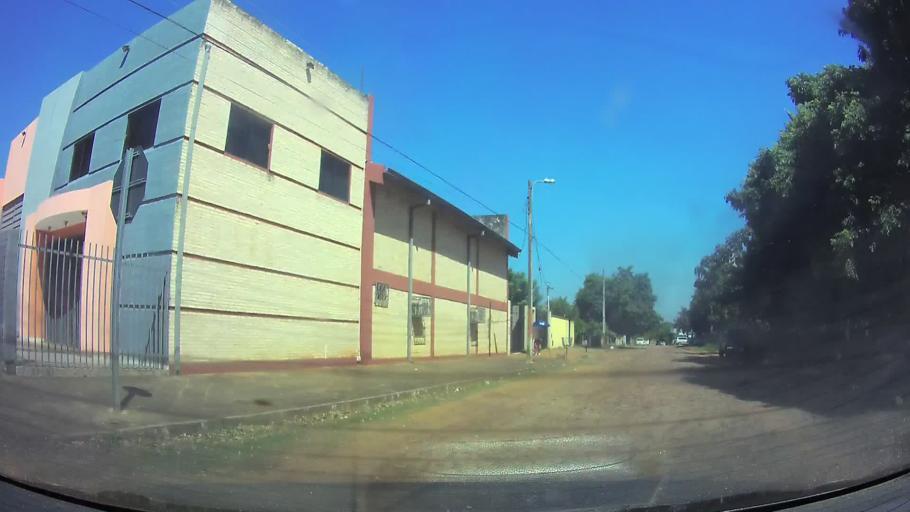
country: PY
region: Central
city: Fernando de la Mora
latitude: -25.3253
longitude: -57.5289
